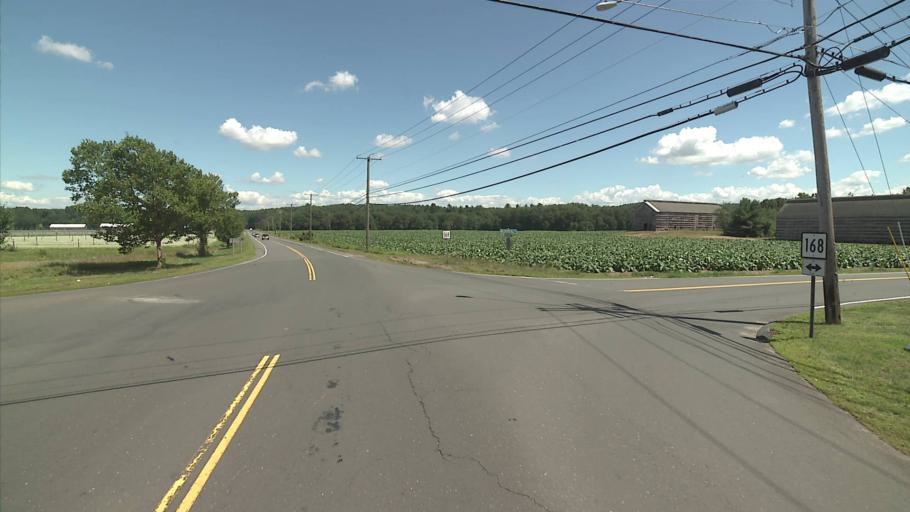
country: US
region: Massachusetts
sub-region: Hampden County
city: Southwick
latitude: 42.0187
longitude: -72.7480
